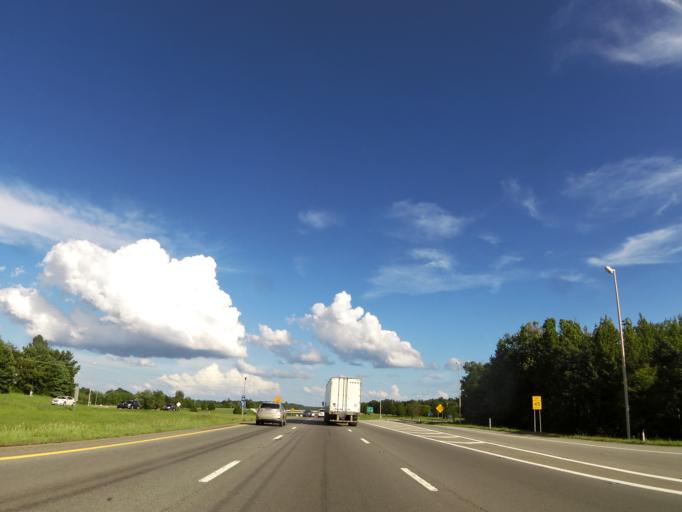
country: US
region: Tennessee
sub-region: Robertson County
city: Coopertown
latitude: 36.3508
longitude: -86.9356
